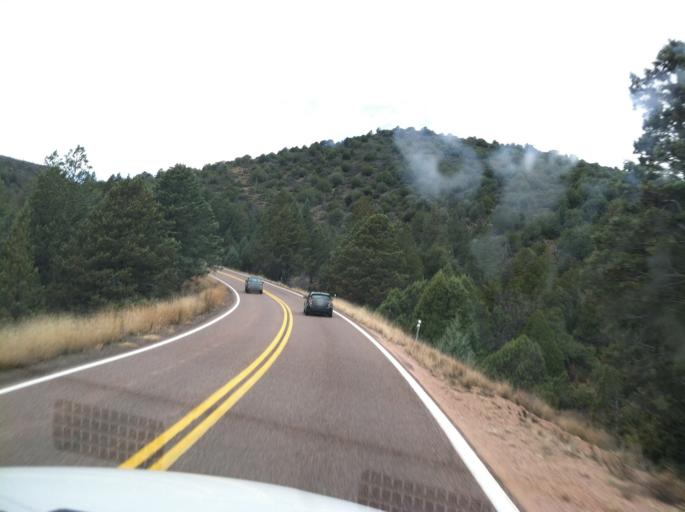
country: US
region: Arizona
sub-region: Gila County
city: Pine
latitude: 34.3186
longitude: -111.3792
